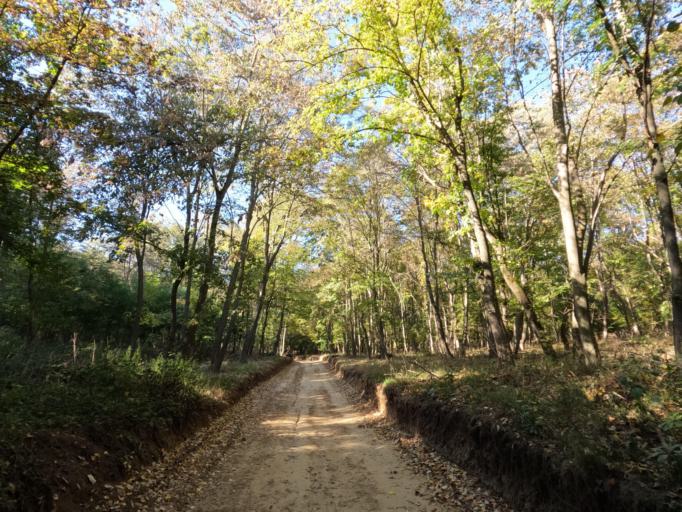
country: HU
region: Tolna
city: Szekszard
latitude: 46.3196
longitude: 18.6584
